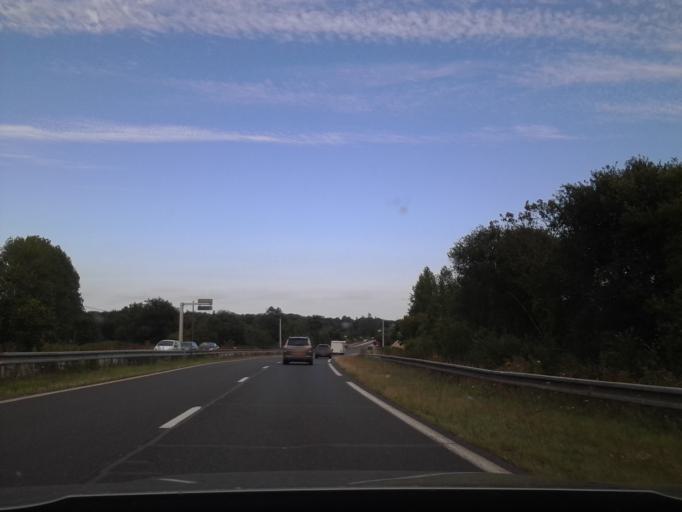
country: FR
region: Lower Normandy
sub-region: Departement de la Manche
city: Valognes
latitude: 49.5313
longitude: -1.5235
